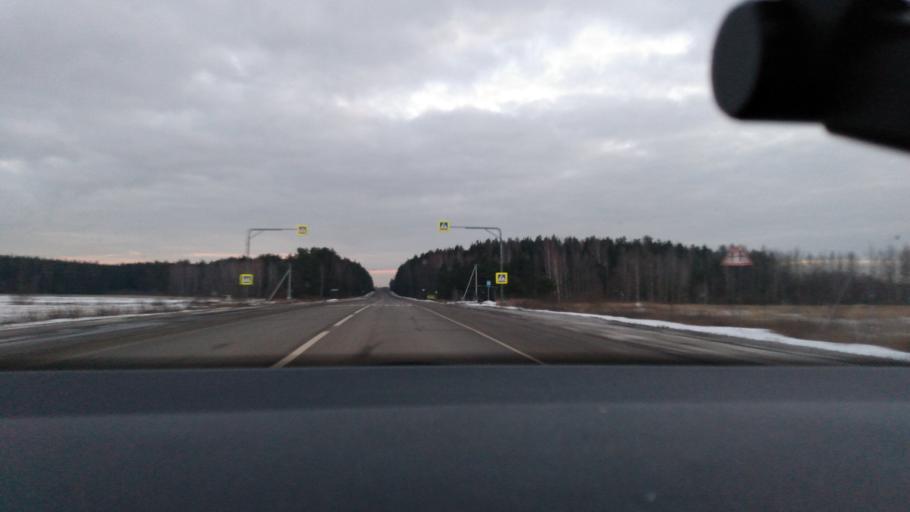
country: RU
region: Moskovskaya
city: Yegor'yevsk
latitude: 55.4343
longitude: 39.0262
